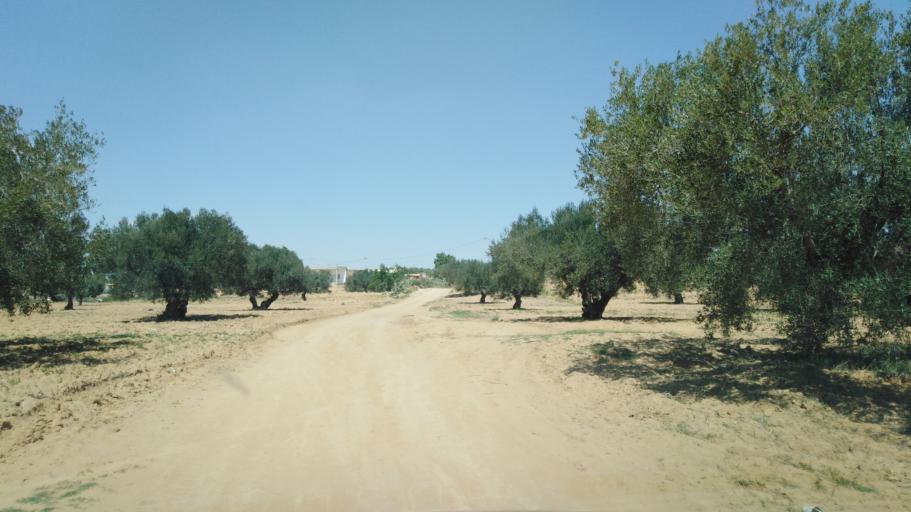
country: TN
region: Safaqis
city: Sfax
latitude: 34.7748
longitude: 10.5276
